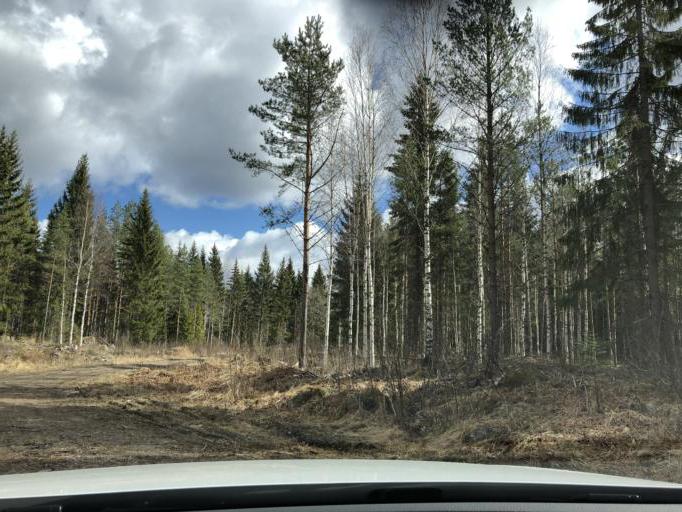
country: SE
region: Uppsala
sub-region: Tierps Kommun
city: Tierp
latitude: 60.3325
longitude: 17.3317
